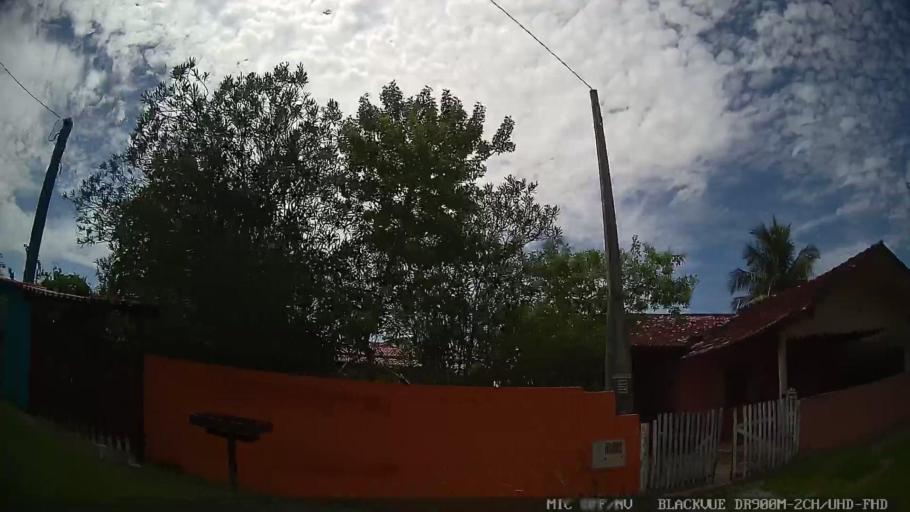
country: BR
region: Sao Paulo
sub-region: Iguape
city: Iguape
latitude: -24.7293
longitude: -47.5192
